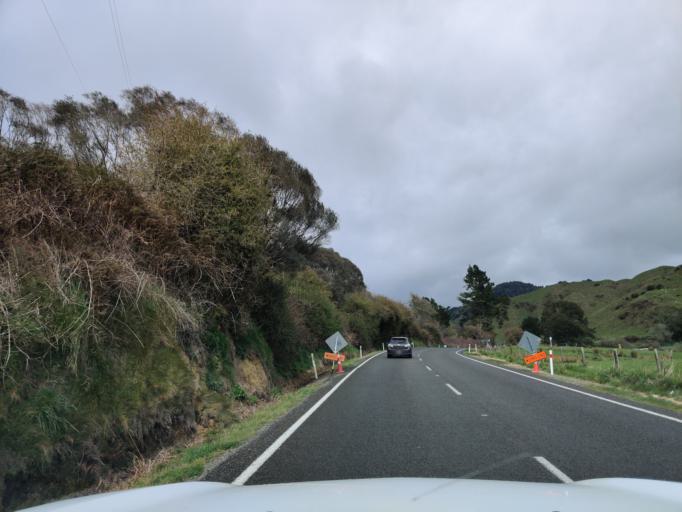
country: NZ
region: Waikato
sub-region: Otorohanga District
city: Otorohanga
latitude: -38.6171
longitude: 175.2185
